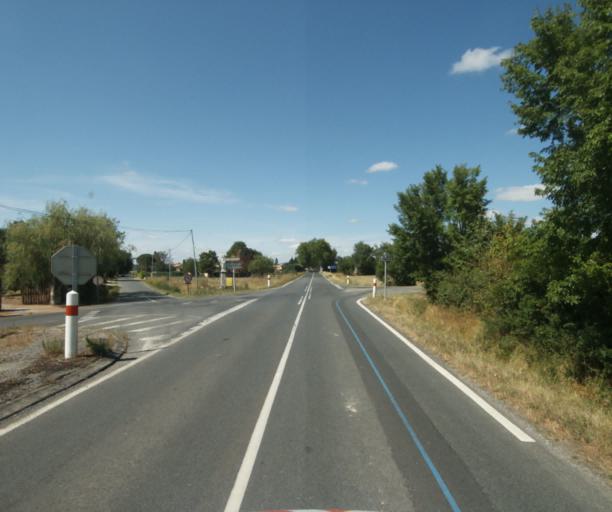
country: FR
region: Midi-Pyrenees
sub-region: Departement de la Haute-Garonne
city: Revel
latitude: 43.4854
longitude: 2.0140
